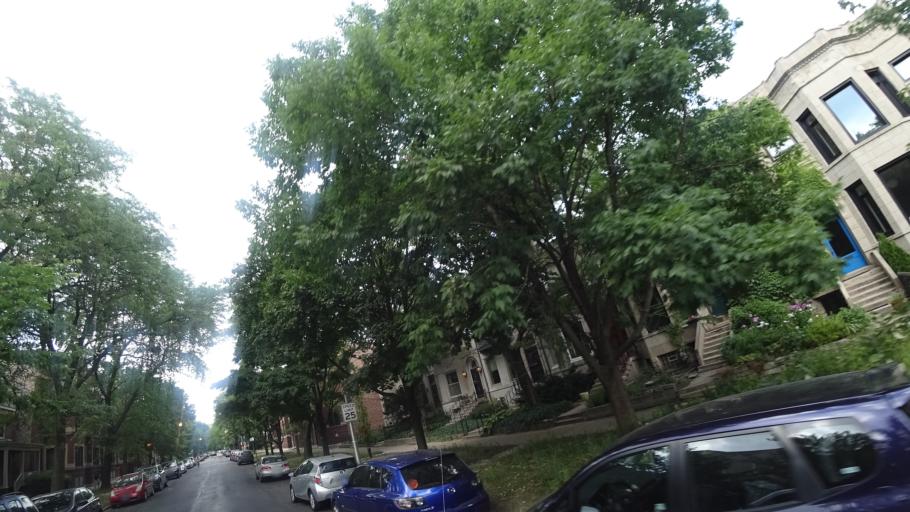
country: US
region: Illinois
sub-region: Cook County
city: Chicago
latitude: 41.7956
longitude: -87.6013
